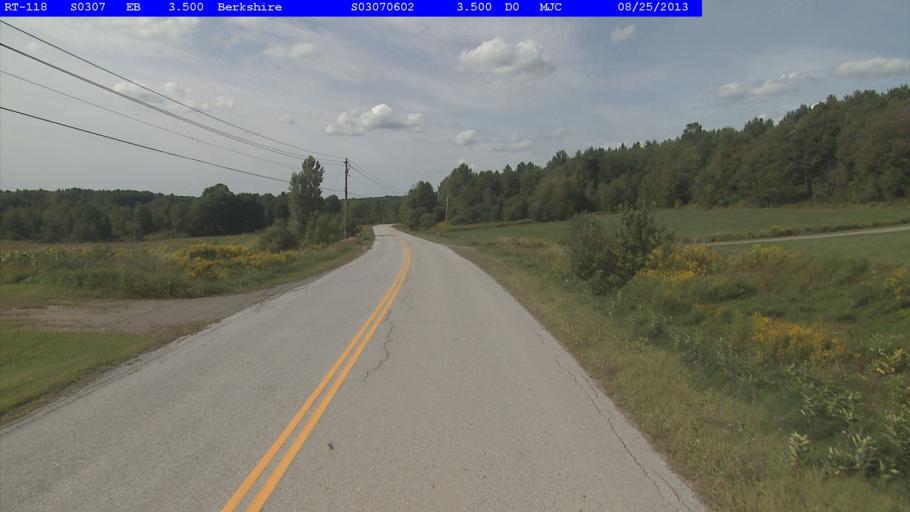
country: US
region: Vermont
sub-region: Franklin County
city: Enosburg Falls
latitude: 44.9658
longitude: -72.7600
